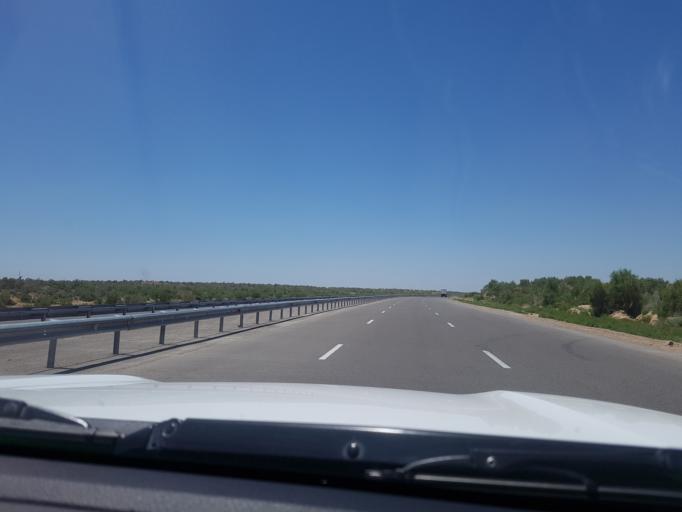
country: TM
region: Mary
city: Mary
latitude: 37.3784
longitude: 61.4759
